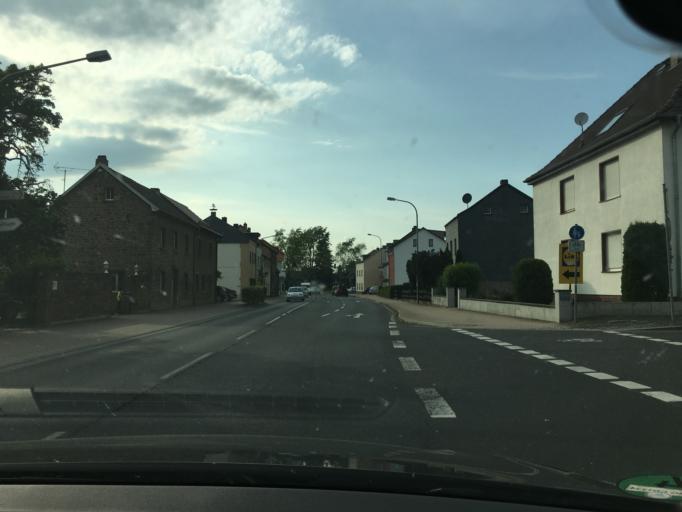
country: DE
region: North Rhine-Westphalia
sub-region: Regierungsbezirk Koln
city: Kreuzau
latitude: 50.7448
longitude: 6.4942
